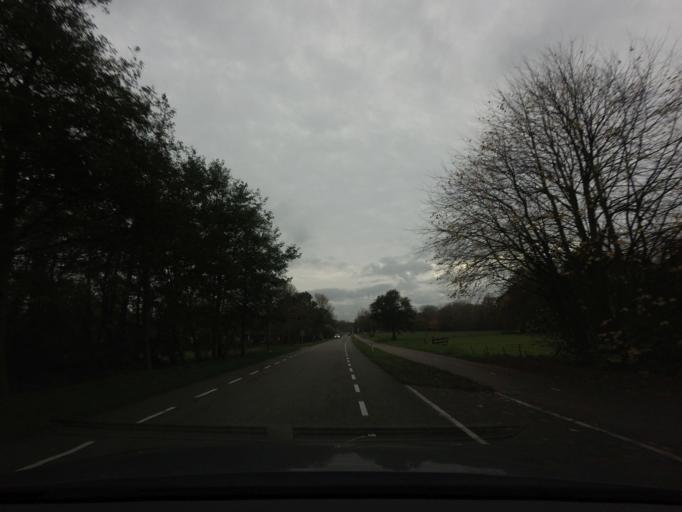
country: NL
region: North Holland
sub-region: Gemeente Bergen
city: Egmond aan Zee
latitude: 52.6443
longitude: 4.6594
